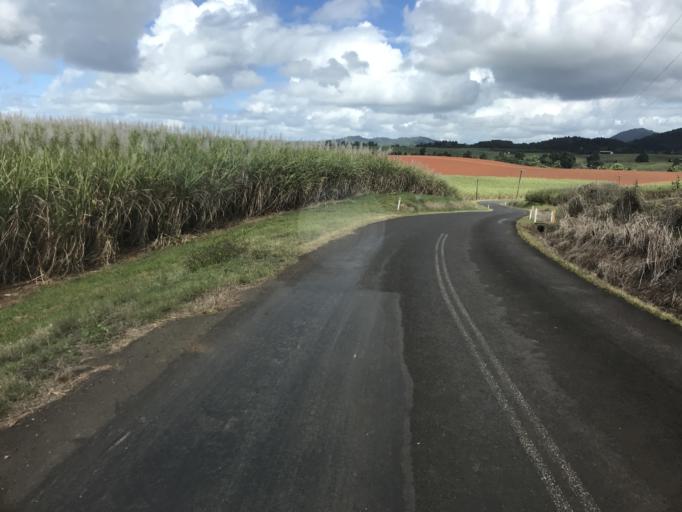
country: AU
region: Queensland
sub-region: Cassowary Coast
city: Innisfail
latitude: -17.5541
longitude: 145.8917
